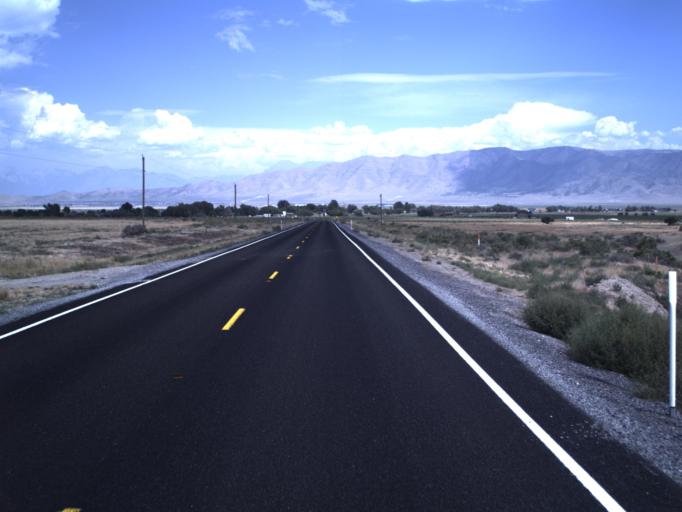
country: US
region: Utah
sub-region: Utah County
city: Eagle Mountain
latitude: 40.2545
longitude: -112.1087
